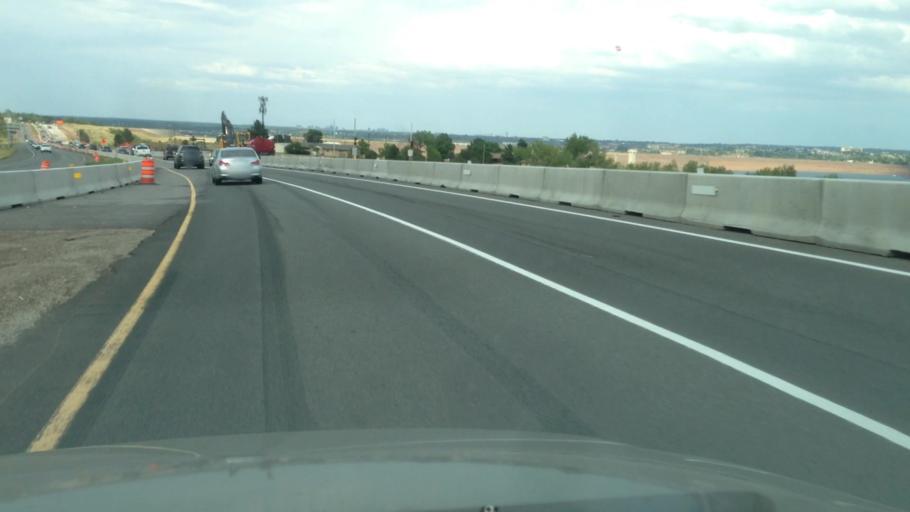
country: US
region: Colorado
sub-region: Jefferson County
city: Ken Caryl
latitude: 39.5546
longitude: -105.0834
